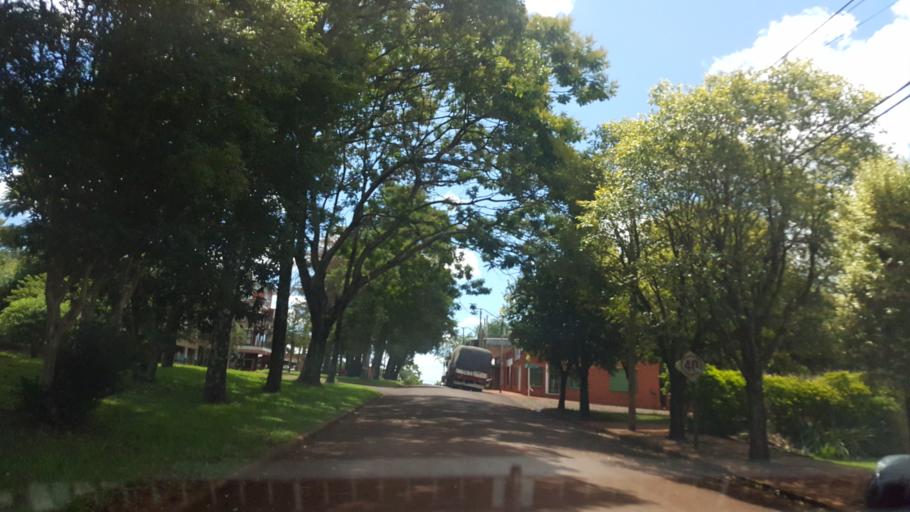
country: AR
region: Misiones
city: Capiovi
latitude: -26.9293
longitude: -55.0557
